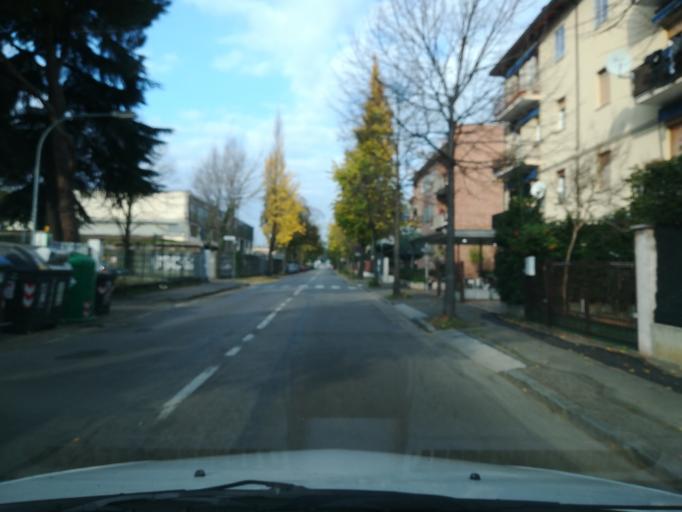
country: IT
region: Emilia-Romagna
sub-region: Provincia di Bologna
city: Imola
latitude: 44.3630
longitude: 11.7187
